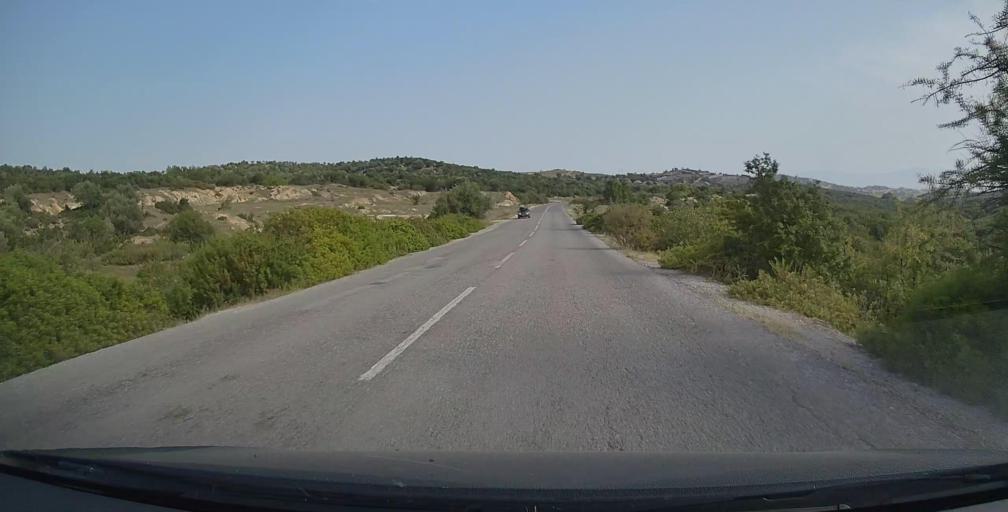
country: GR
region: Central Macedonia
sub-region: Nomos Chalkidikis
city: Sykia
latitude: 40.0102
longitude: 23.9831
